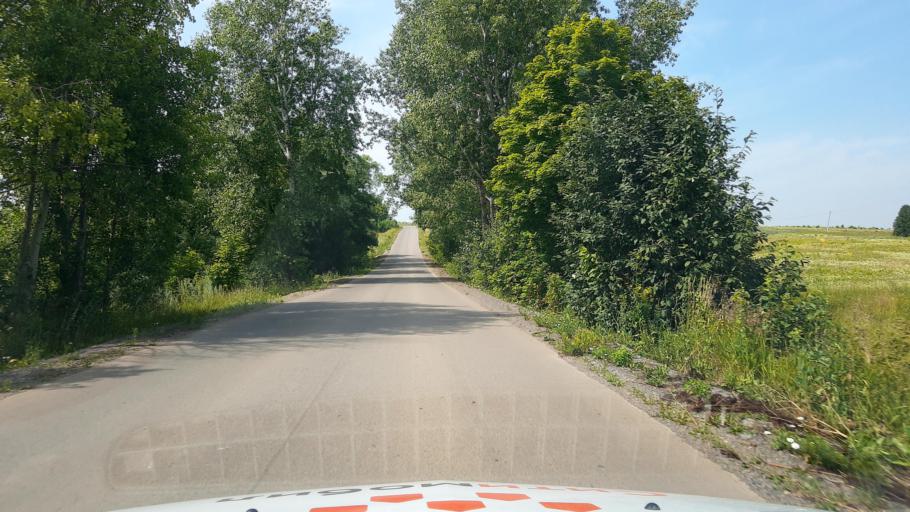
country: RU
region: Bashkortostan
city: Iglino
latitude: 54.8978
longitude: 56.2733
